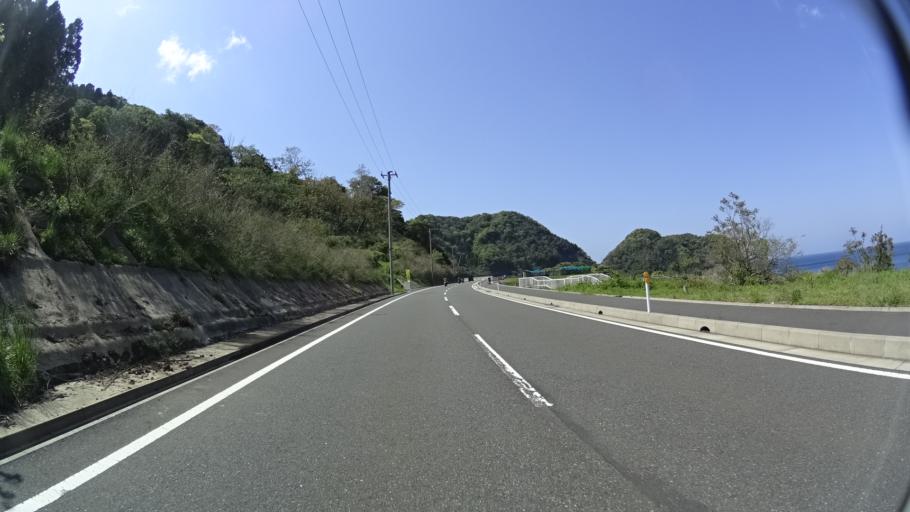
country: JP
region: Kyoto
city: Miyazu
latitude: 35.7470
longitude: 135.2534
